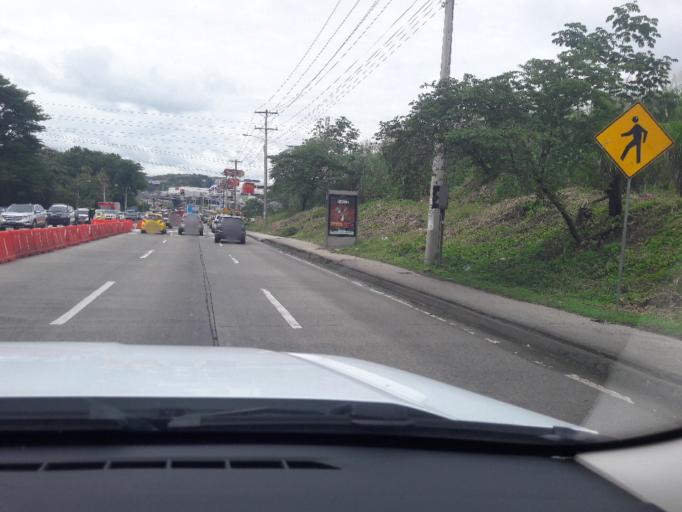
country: PA
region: Panama
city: Panama
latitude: 9.0261
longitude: -79.5290
